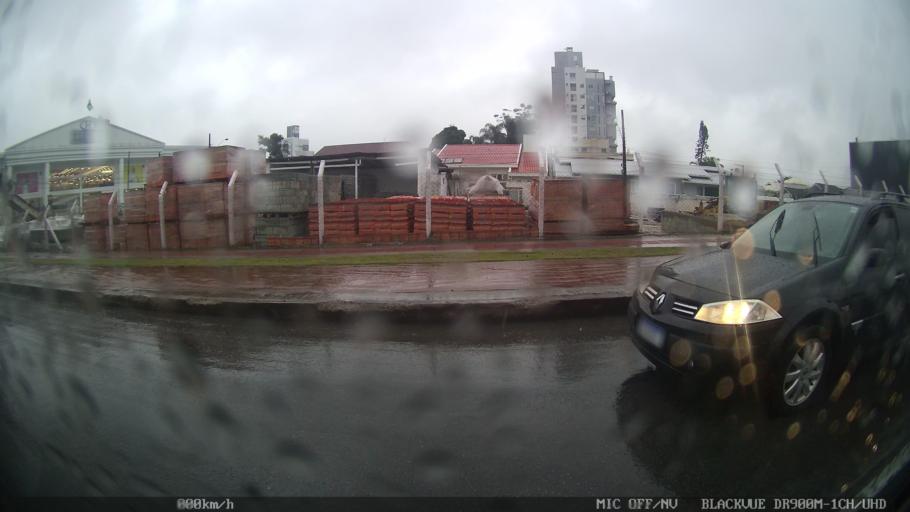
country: BR
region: Santa Catarina
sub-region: Itajai
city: Itajai
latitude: -26.9102
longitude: -48.6835
